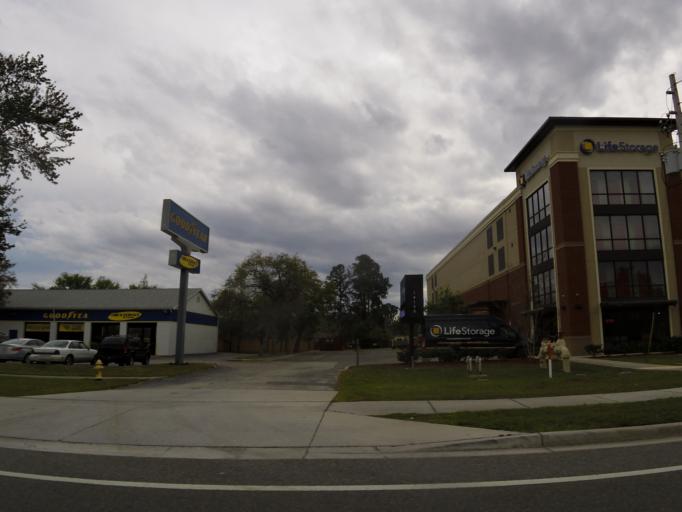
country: US
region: Florida
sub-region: Duval County
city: Jacksonville Beach
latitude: 30.2877
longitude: -81.4442
